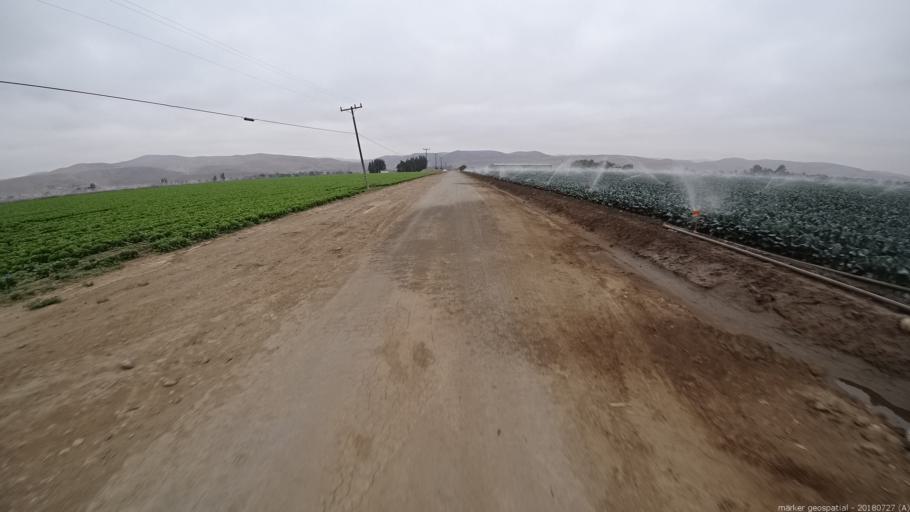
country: US
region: California
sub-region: Monterey County
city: Greenfield
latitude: 36.3381
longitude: -121.2281
